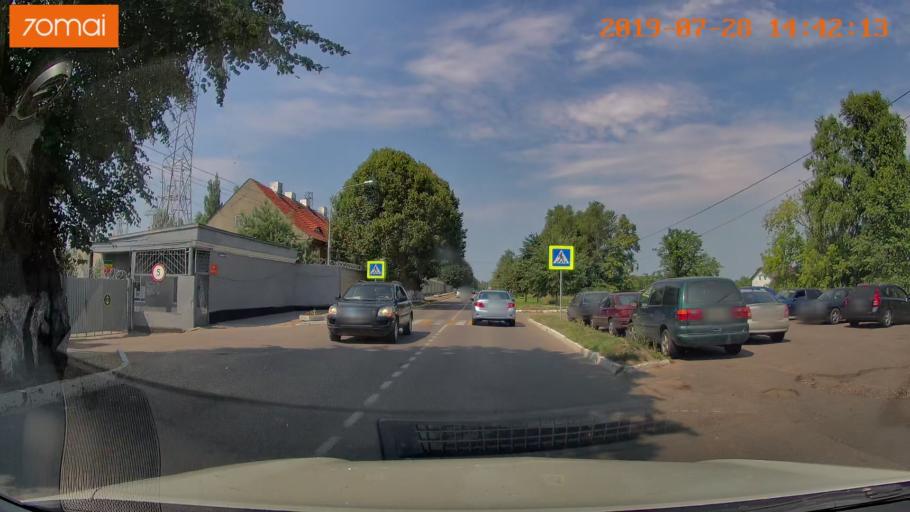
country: RU
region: Kaliningrad
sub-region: Gorod Kaliningrad
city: Yantarnyy
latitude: 54.8586
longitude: 19.9430
